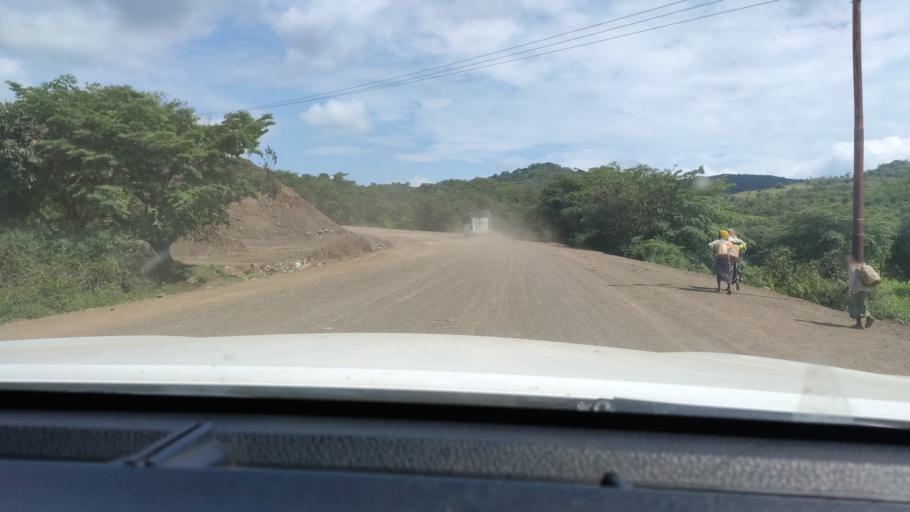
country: ET
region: Southern Nations, Nationalities, and People's Region
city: Felege Neway
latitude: 6.3906
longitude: 37.0620
